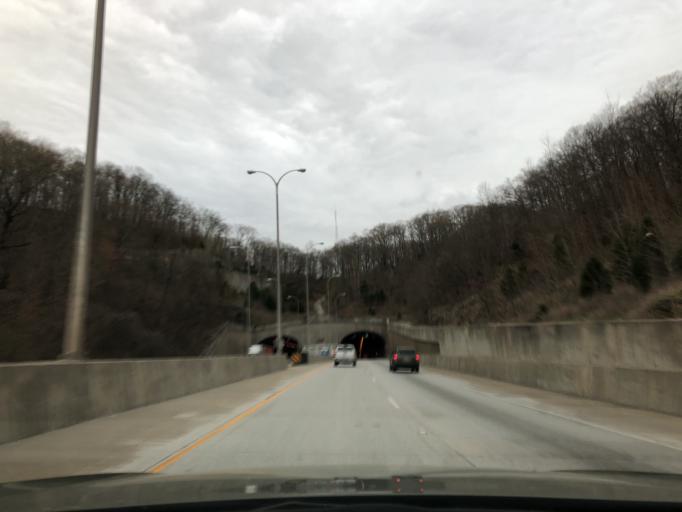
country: US
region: Arkansas
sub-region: Washington County
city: West Fork
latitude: 35.7716
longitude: -94.1871
